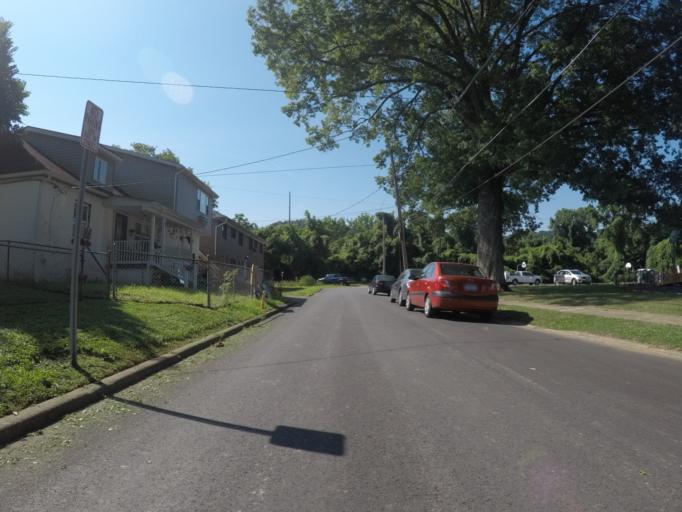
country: US
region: West Virginia
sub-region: Cabell County
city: Huntington
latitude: 38.4049
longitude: -82.4819
